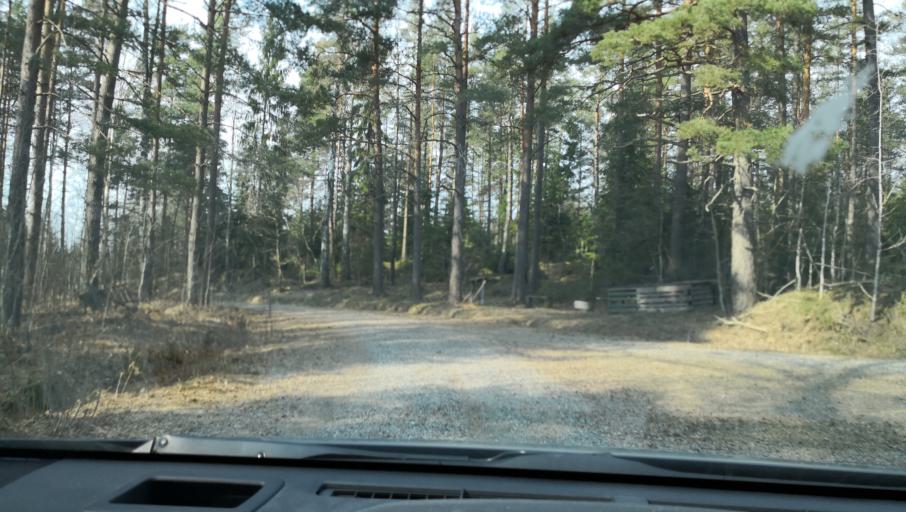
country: SE
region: OErebro
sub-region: Lindesbergs Kommun
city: Frovi
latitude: 59.3822
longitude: 15.4132
